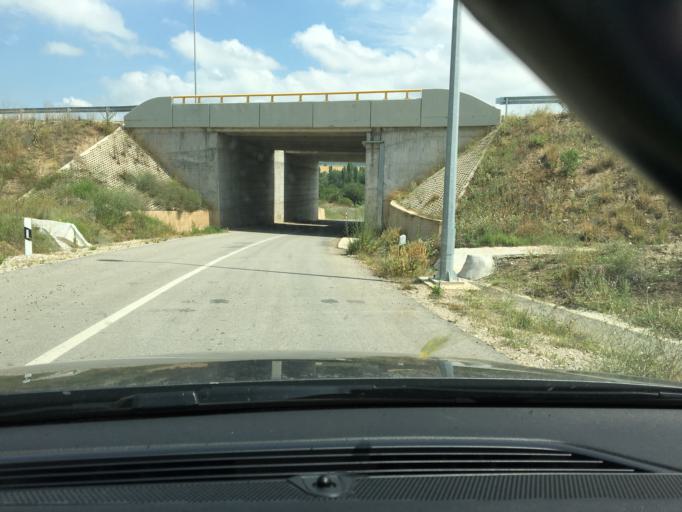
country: MK
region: Sveti Nikole
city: Gorobinci
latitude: 41.9163
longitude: 21.8786
